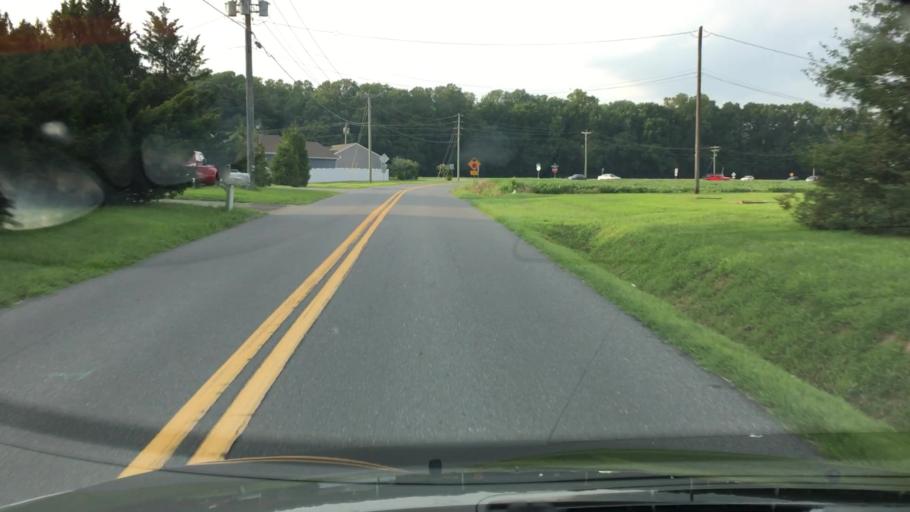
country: US
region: Delaware
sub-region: Sussex County
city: Selbyville
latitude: 38.4767
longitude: -75.1403
